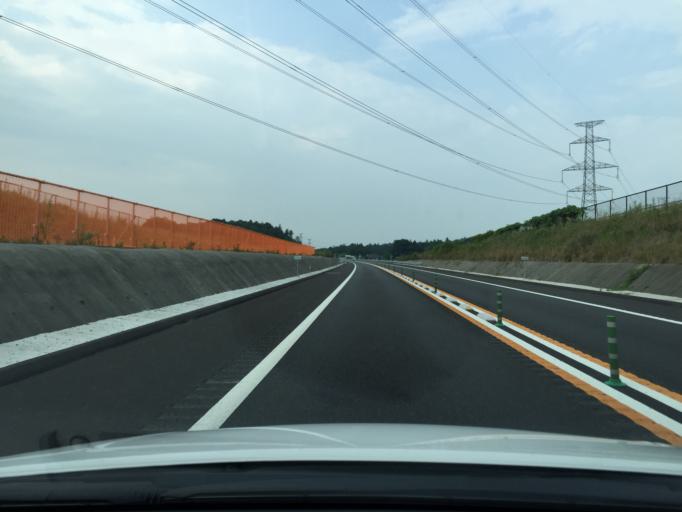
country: JP
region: Fukushima
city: Namie
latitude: 37.5139
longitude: 140.9438
